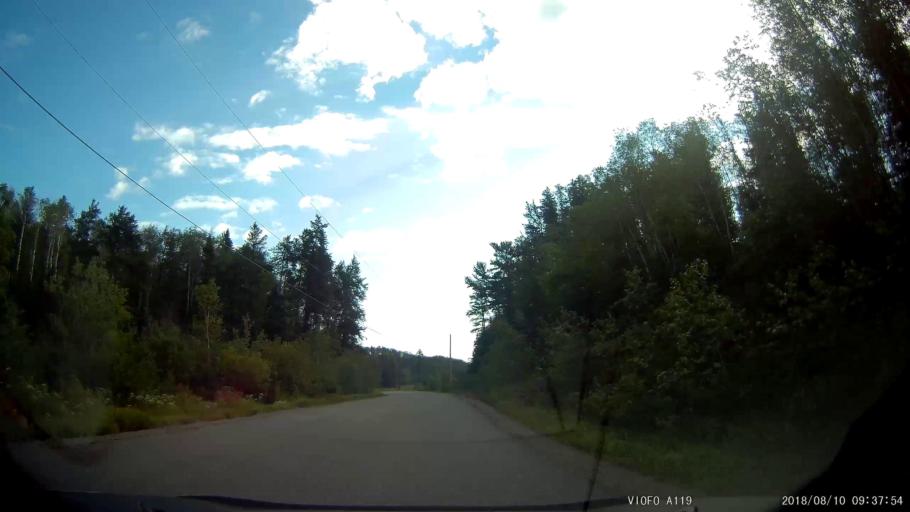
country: CA
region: Ontario
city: Rayside-Balfour
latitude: 46.6158
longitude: -81.4677
